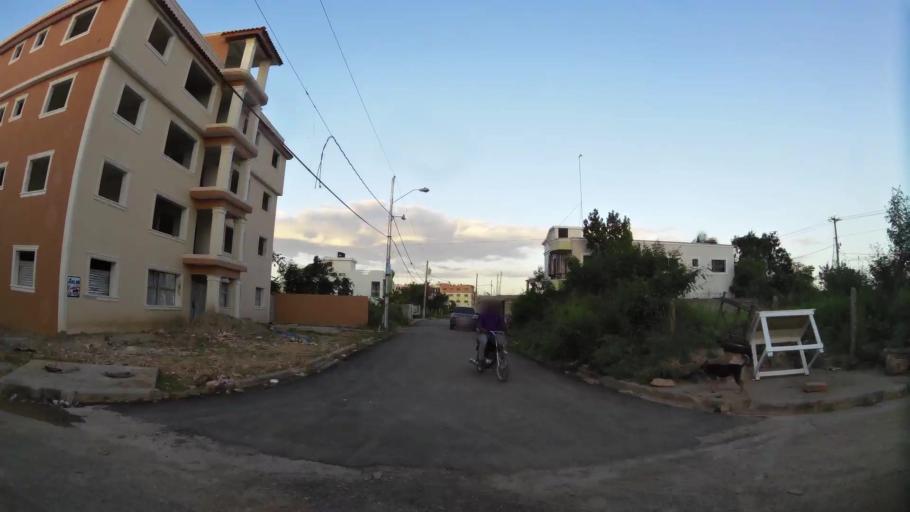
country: DO
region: Santo Domingo
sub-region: Santo Domingo
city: Santo Domingo Este
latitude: 18.4869
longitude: -69.8196
